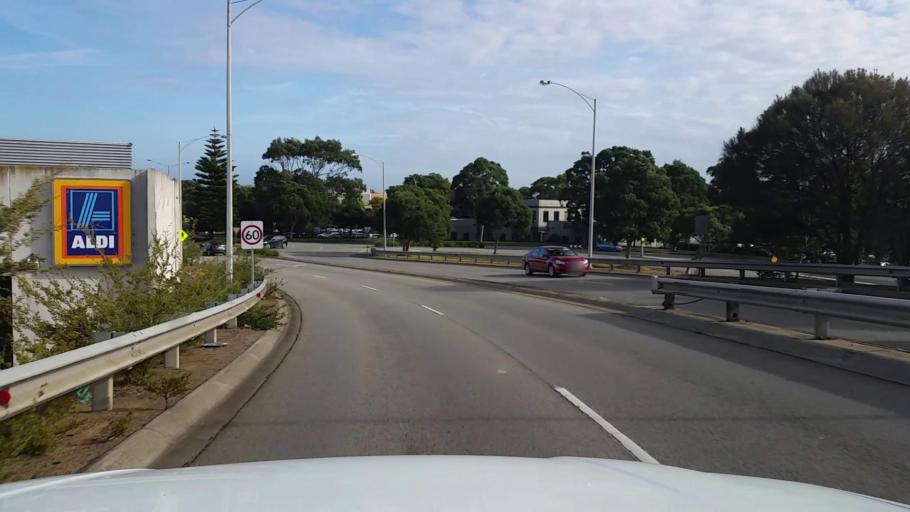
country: AU
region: Victoria
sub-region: Frankston
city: Frankston
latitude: -38.1398
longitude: 145.1268
